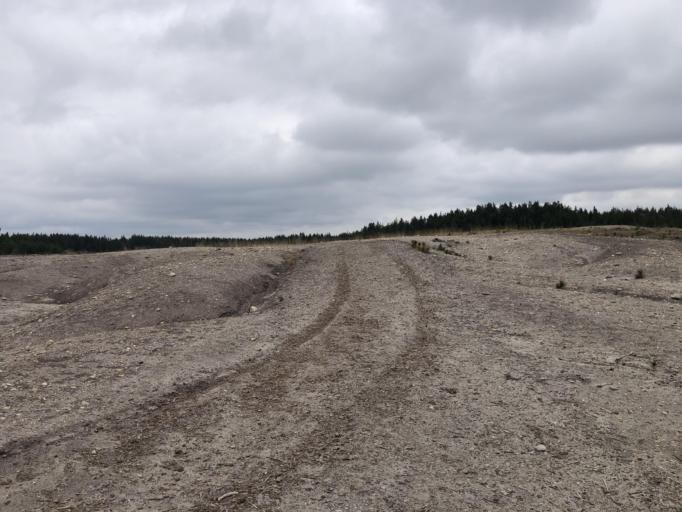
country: DK
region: Central Jutland
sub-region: Ikast-Brande Kommune
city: Brande
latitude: 56.0160
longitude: 9.0733
